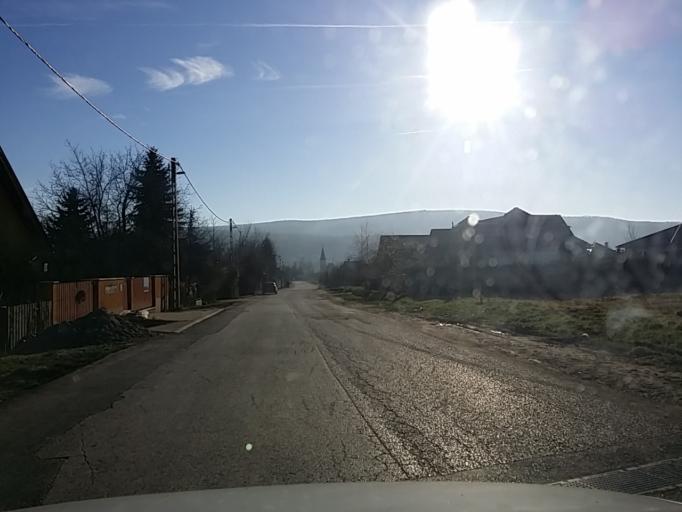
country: HU
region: Pest
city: Pilisszentivan
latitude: 47.5818
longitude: 18.8840
